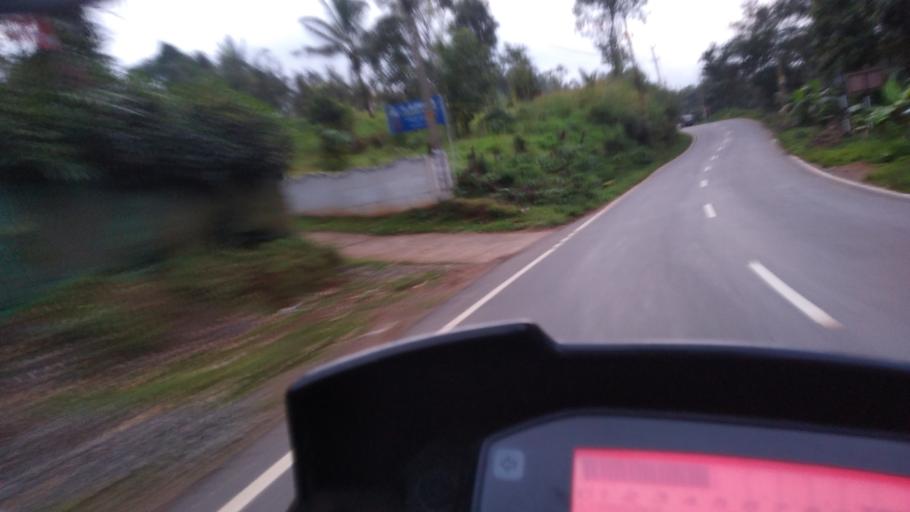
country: IN
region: Kerala
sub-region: Idukki
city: Munnar
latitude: 9.9687
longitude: 77.1281
